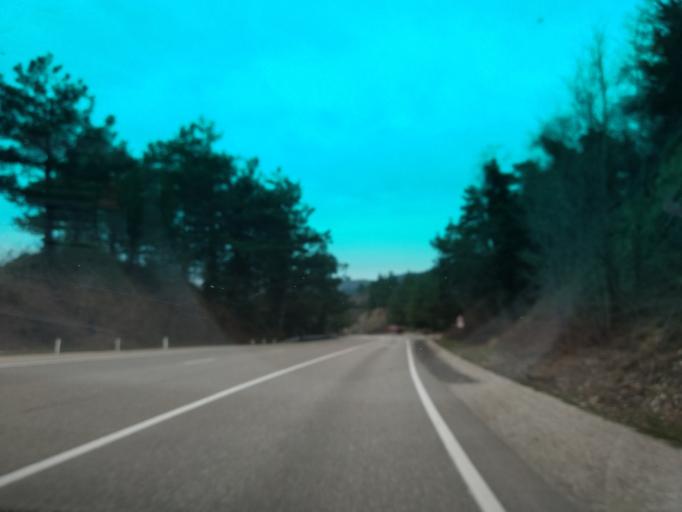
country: RU
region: Krasnodarskiy
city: Ol'ginka
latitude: 44.1828
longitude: 38.9276
